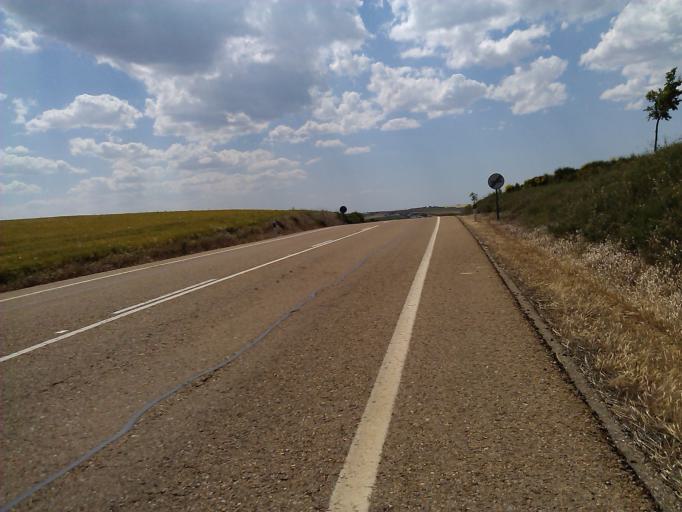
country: ES
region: Castille and Leon
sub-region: Provincia de Palencia
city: Moratinos
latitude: 42.3638
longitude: -4.9377
